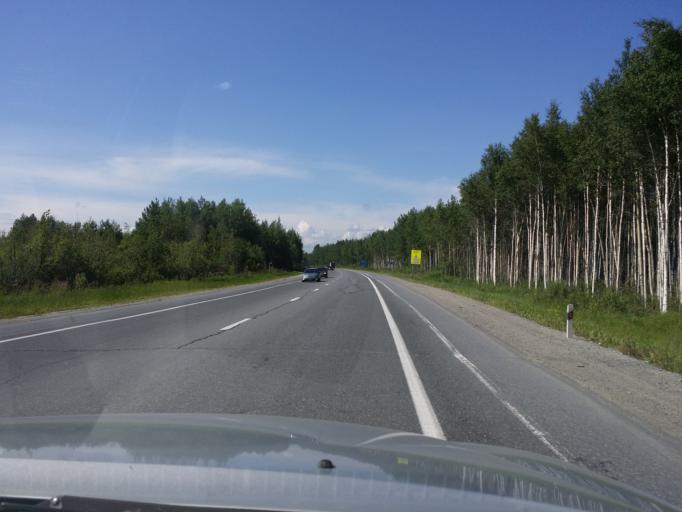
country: RU
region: Khanty-Mansiyskiy Avtonomnyy Okrug
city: Nizhnevartovsk
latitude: 61.0138
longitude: 76.3962
